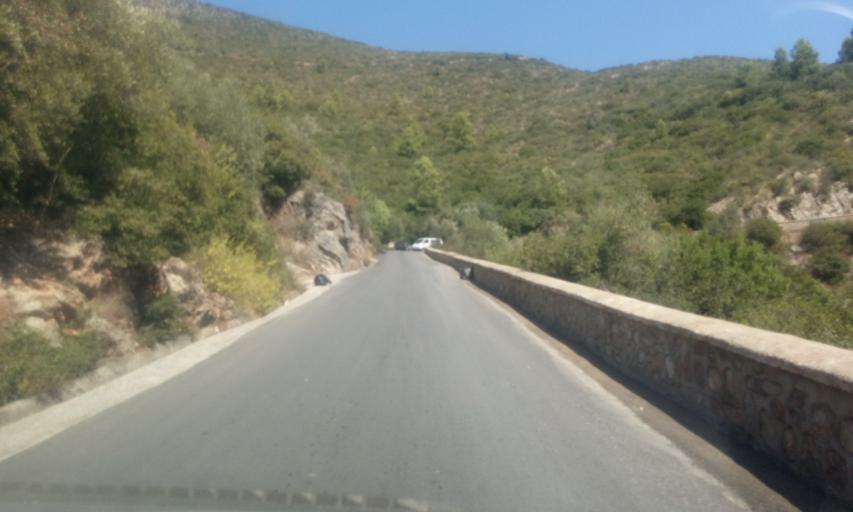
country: DZ
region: Bejaia
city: Bejaia
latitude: 36.7631
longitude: 5.0866
